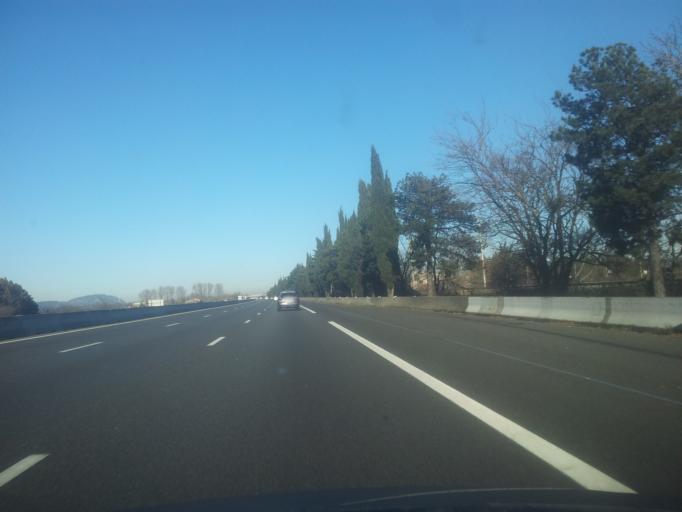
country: FR
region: Rhone-Alpes
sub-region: Departement de la Drome
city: Etoile-sur-Rhone
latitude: 44.8195
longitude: 4.8586
